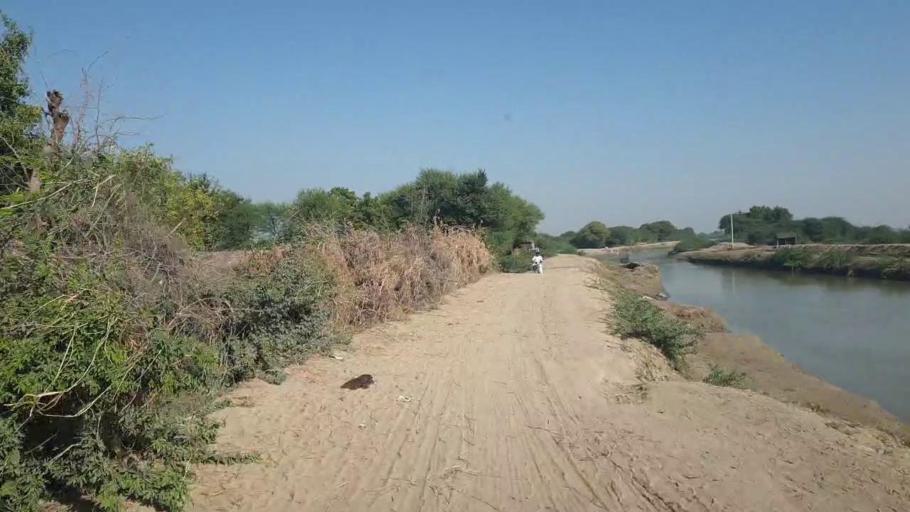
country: PK
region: Sindh
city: Badin
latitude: 24.7221
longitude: 68.8029
